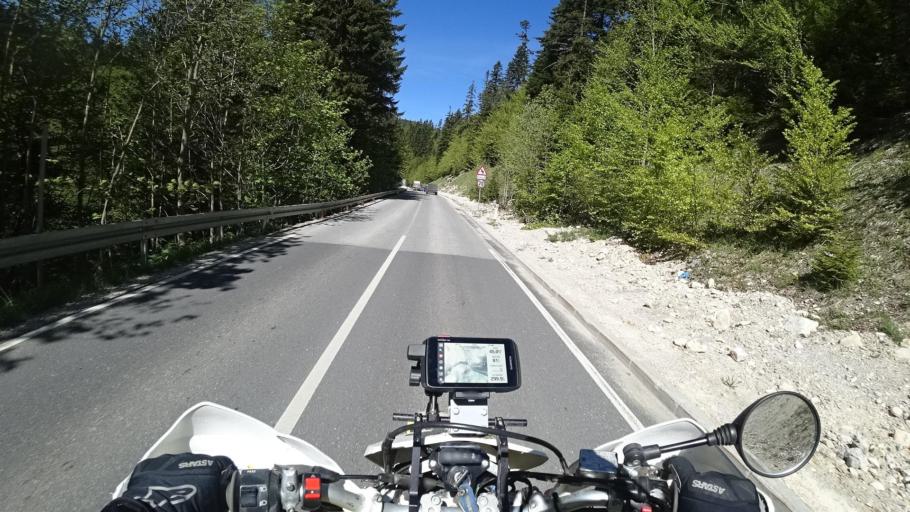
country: BA
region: Federation of Bosnia and Herzegovina
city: Gracanica
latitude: 43.7373
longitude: 18.2780
